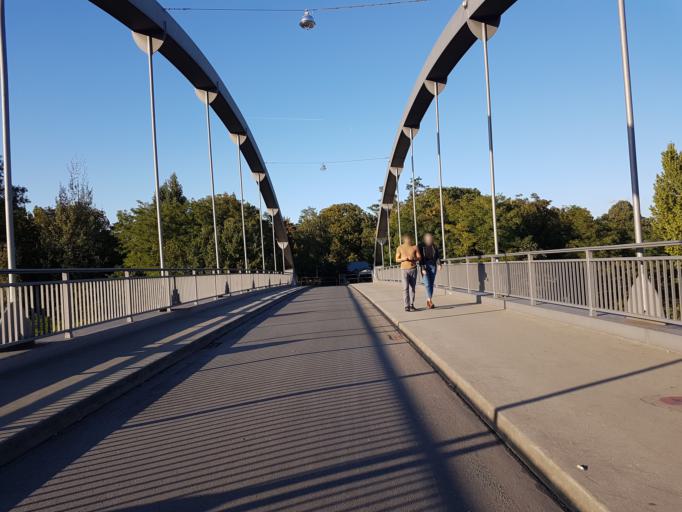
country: DE
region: Lower Saxony
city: Hannover
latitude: 52.4051
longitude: 9.7480
